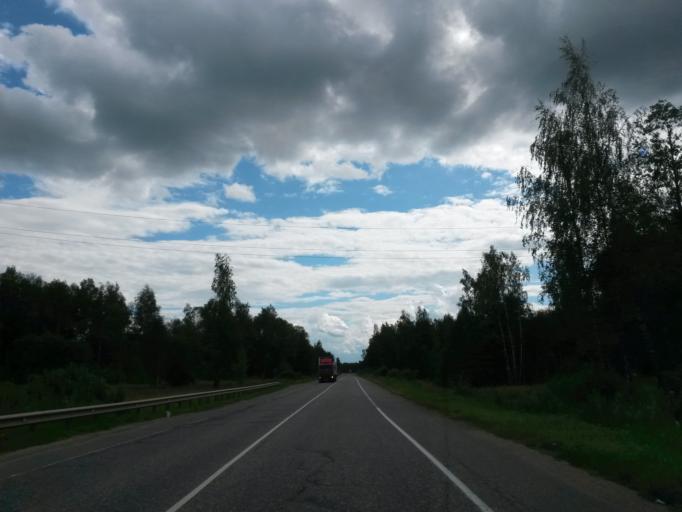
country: RU
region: Ivanovo
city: Pistsovo
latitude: 57.0872
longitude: 40.6696
